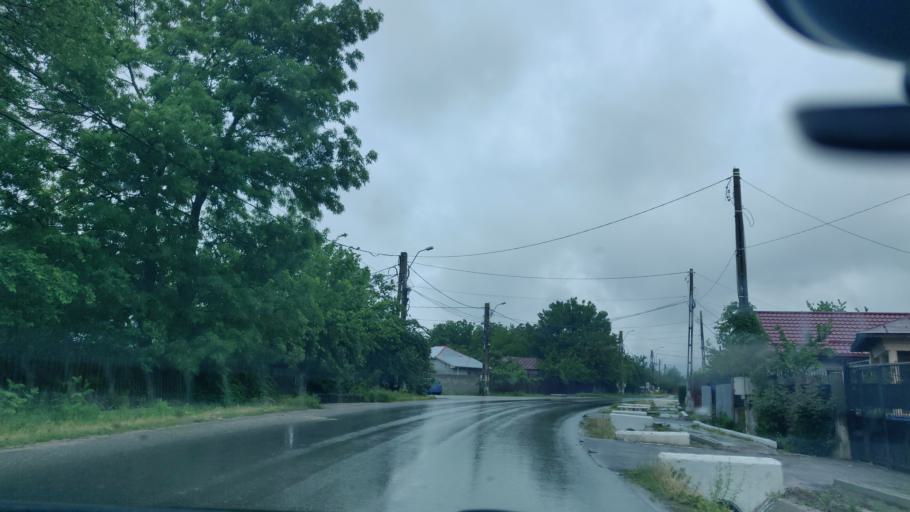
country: RO
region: Giurgiu
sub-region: Comuna Bulbucata
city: Bulbucata
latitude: 44.2758
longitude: 25.8231
